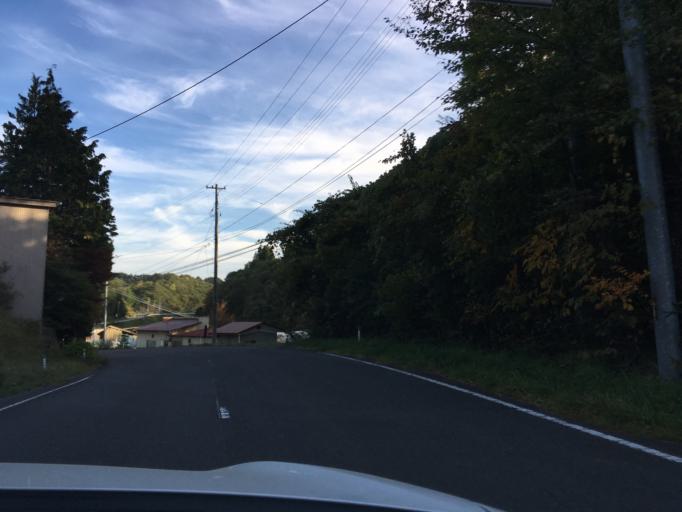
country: JP
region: Fukushima
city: Ishikawa
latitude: 37.1927
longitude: 140.5390
